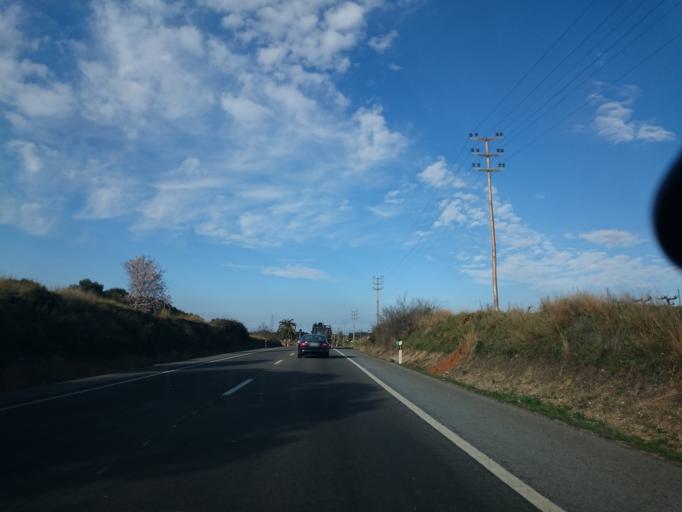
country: ES
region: Catalonia
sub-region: Provincia de Barcelona
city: Castellet
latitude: 41.2741
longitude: 1.6101
